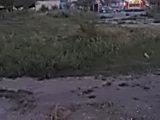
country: RU
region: Orenburg
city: Novotroitsk
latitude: 51.1924
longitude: 58.2918
